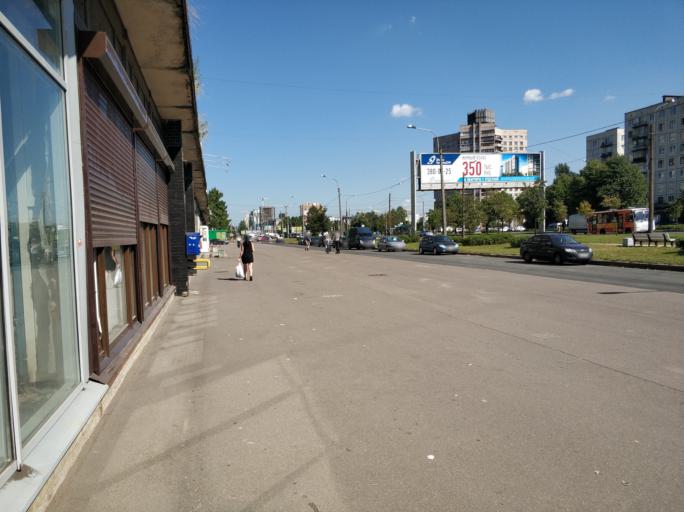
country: RU
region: Leningrad
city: Akademicheskoe
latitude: 60.0194
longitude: 30.4032
